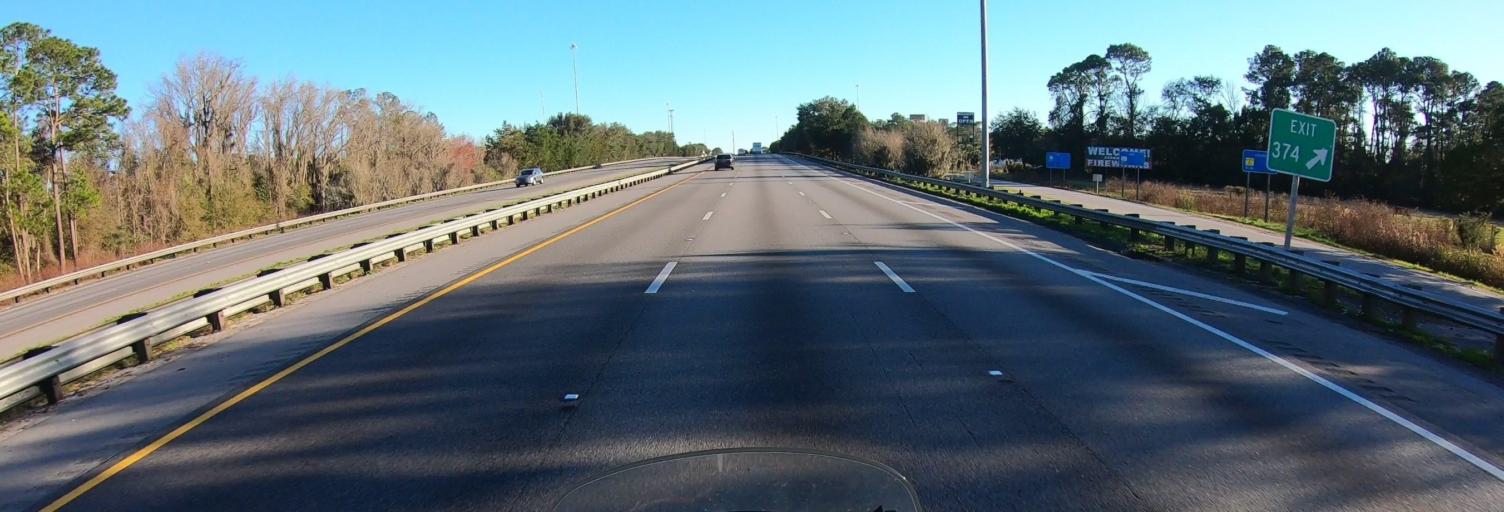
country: US
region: Florida
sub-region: Alachua County
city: Gainesville
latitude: 29.5003
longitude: -82.2954
